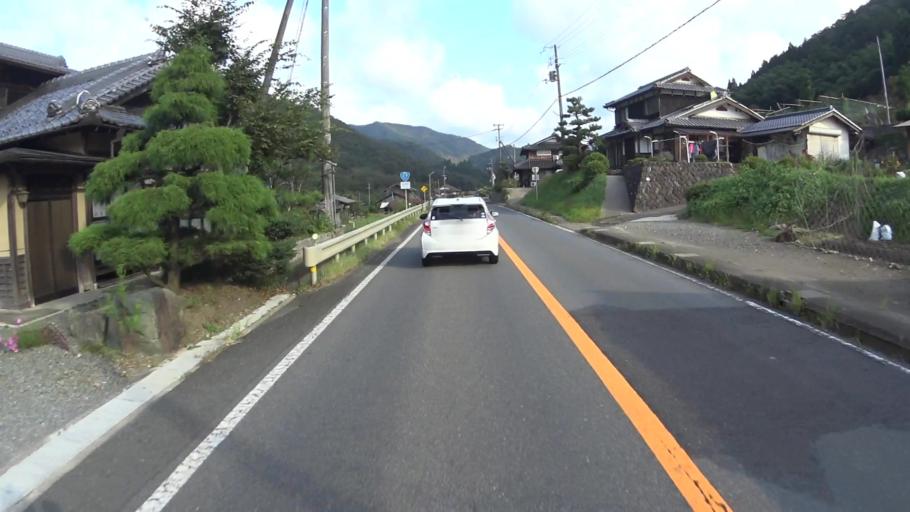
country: JP
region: Kyoto
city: Ayabe
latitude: 35.2337
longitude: 135.4134
